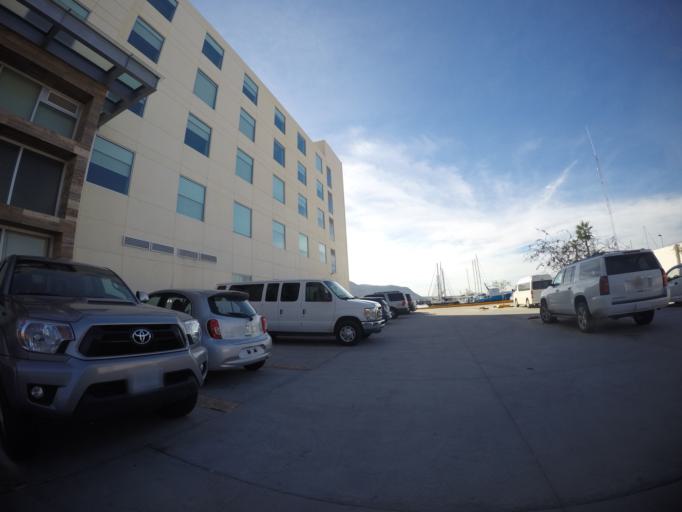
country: MX
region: Baja California Sur
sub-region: La Paz
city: La Paz
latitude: 24.1882
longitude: -110.2941
